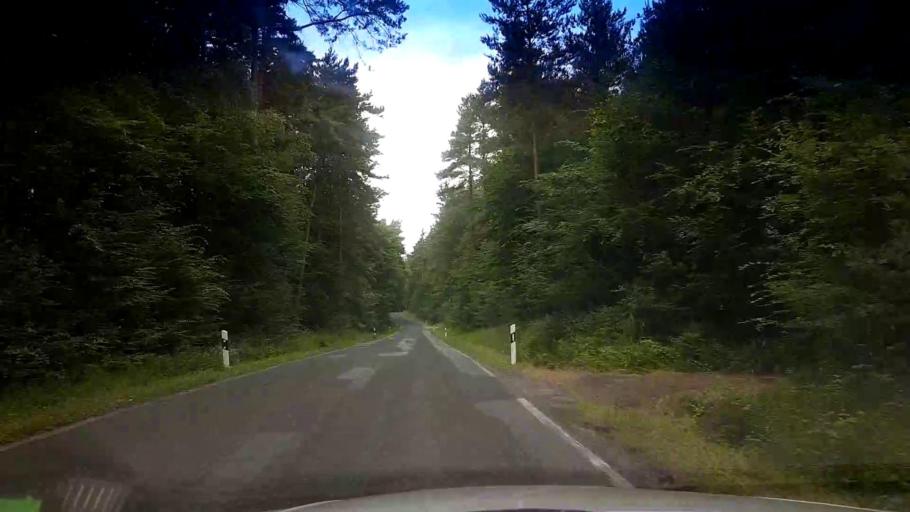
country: DE
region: Bavaria
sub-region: Upper Franconia
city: Oberhaid
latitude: 49.9462
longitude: 10.8154
